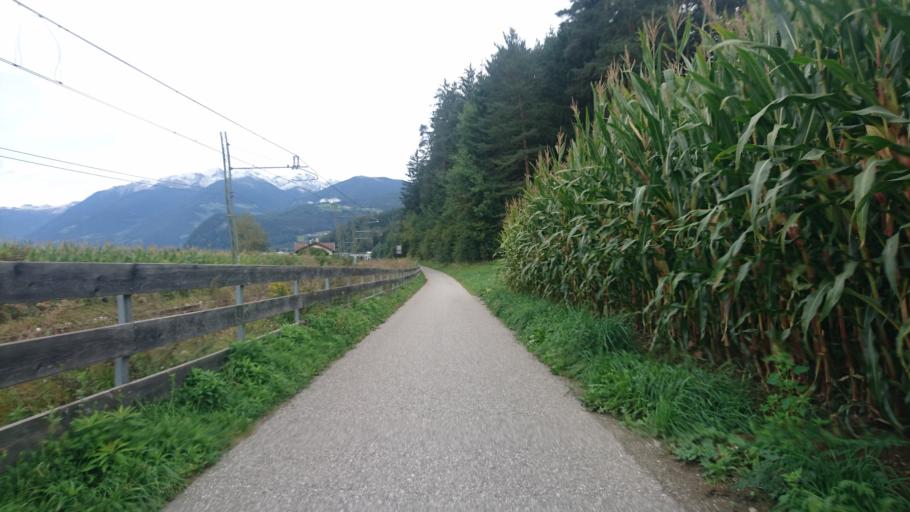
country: IT
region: Trentino-Alto Adige
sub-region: Bolzano
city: San Lorenzo di Sebato
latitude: 46.7831
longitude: 11.9231
